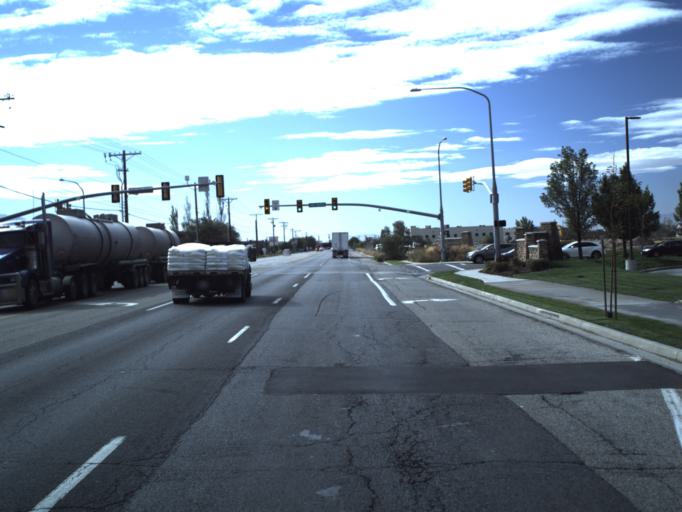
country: US
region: Utah
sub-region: Davis County
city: North Salt Lake
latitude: 40.8536
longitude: -111.9299
